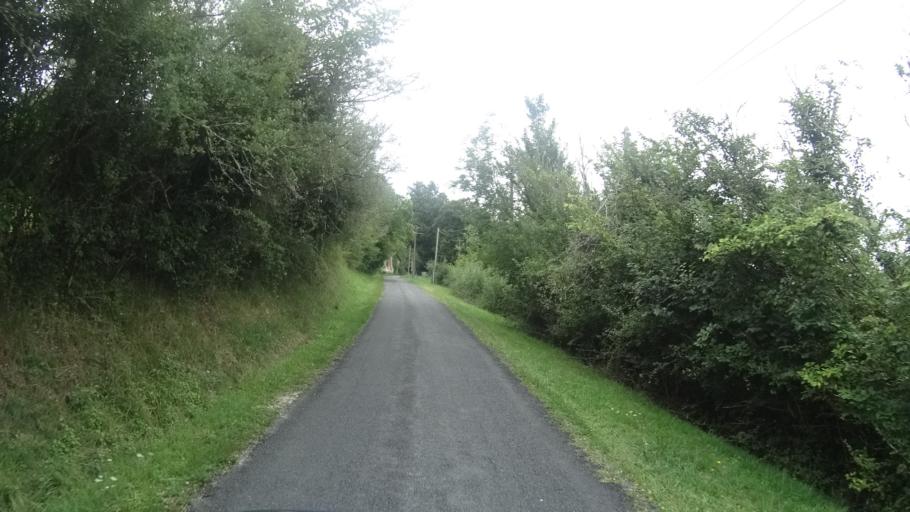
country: FR
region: Aquitaine
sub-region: Departement de la Dordogne
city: Neuvic
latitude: 45.0380
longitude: 0.5222
